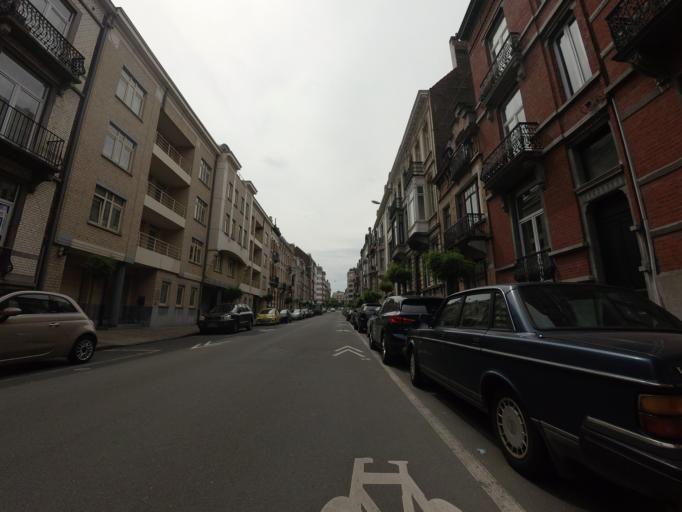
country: BE
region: Brussels Capital
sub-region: Bruxelles-Capitale
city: Brussels
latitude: 50.8216
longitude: 4.3631
